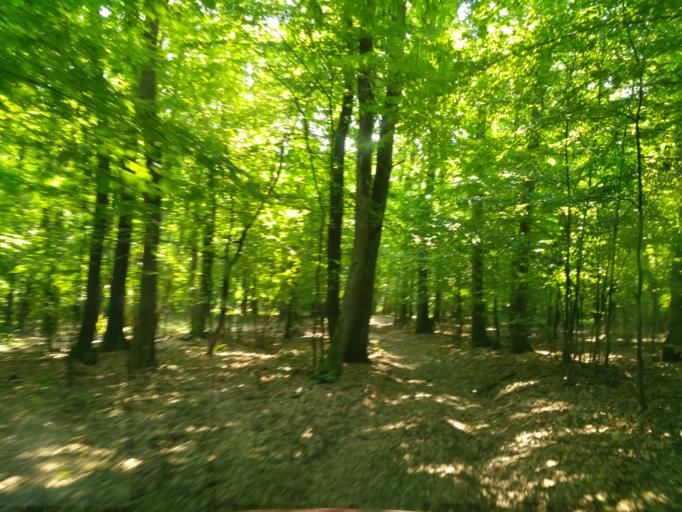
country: SK
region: Kosicky
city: Moldava nad Bodvou
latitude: 48.6425
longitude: 21.0402
